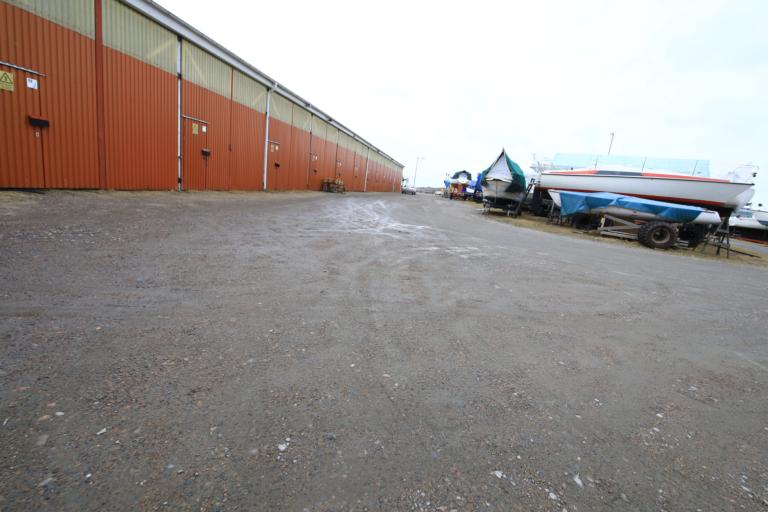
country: SE
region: Halland
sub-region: Kungsbacka Kommun
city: Frillesas
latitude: 57.2425
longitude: 12.1171
